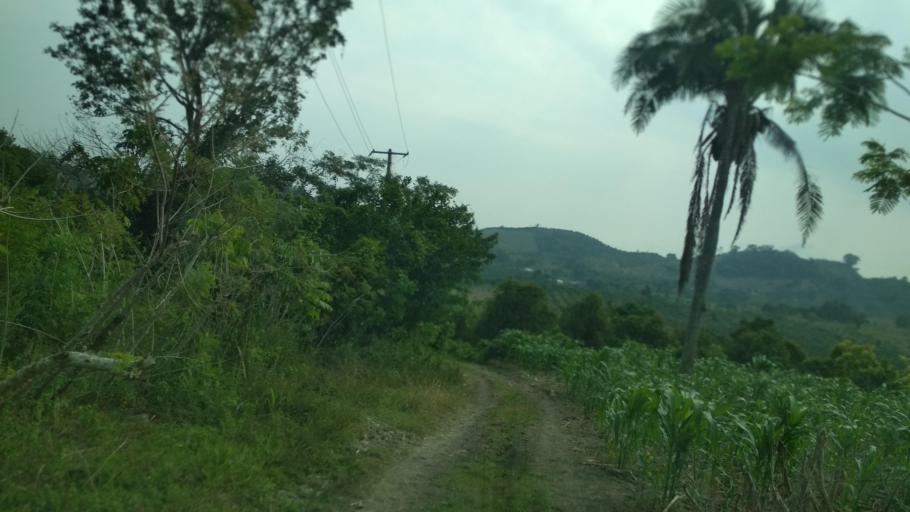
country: MM
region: Kayah
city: Loikaw
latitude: 20.2048
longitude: 97.3215
